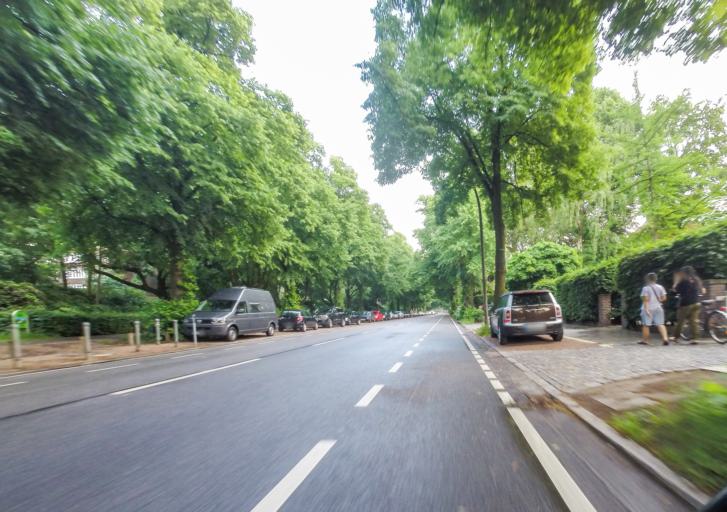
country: DE
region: Hamburg
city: Winterhude
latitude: 53.5979
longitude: 9.9940
